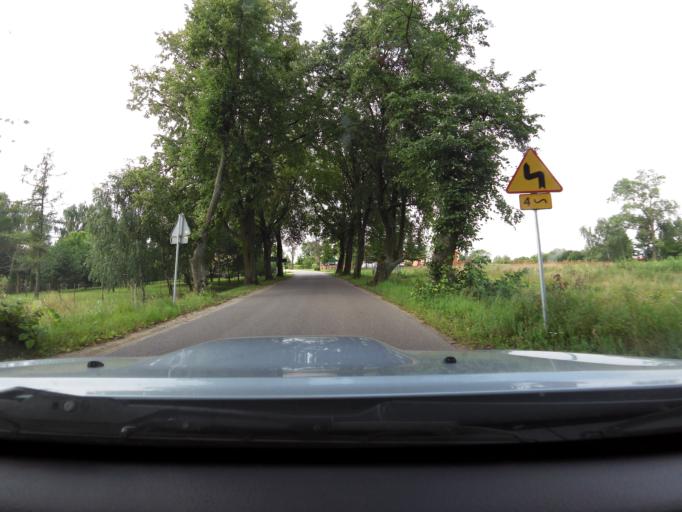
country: PL
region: Warmian-Masurian Voivodeship
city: Gierloz
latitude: 54.0854
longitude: 21.4450
